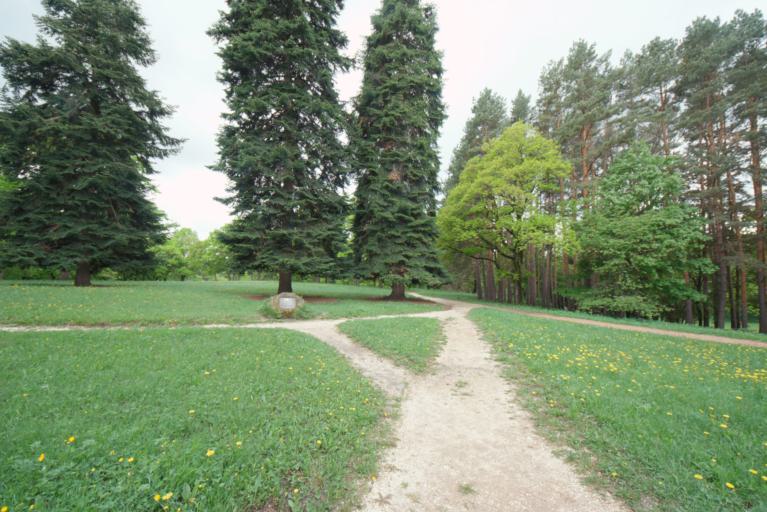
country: RU
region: Stavropol'skiy
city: Kislovodsk
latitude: 43.8971
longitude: 42.7328
